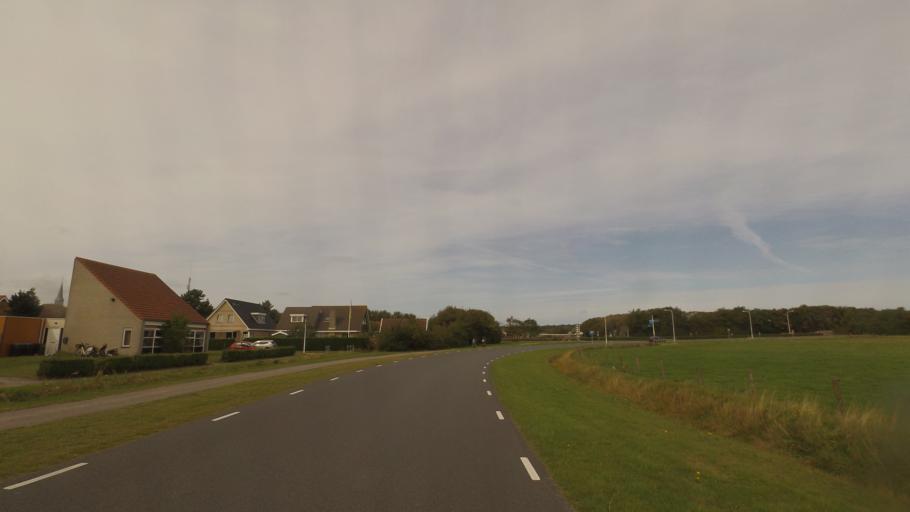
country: NL
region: Friesland
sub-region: Gemeente Ameland
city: Nes
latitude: 53.4457
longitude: 5.7816
